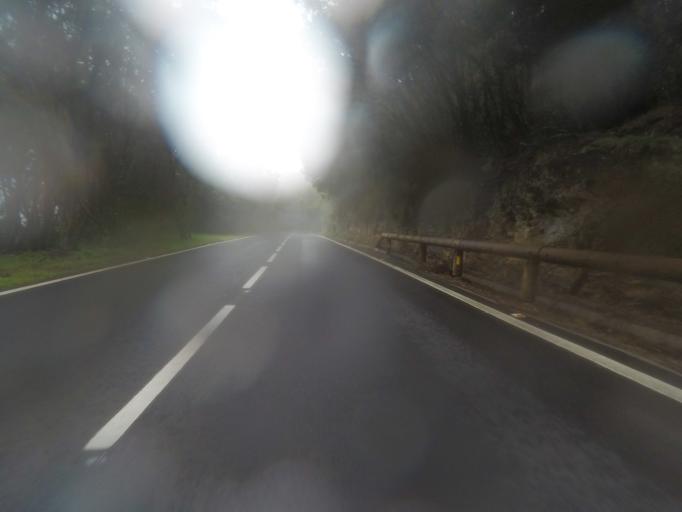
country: ES
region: Canary Islands
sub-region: Provincia de Santa Cruz de Tenerife
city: Vallehermosa
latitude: 28.1279
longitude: -17.2645
